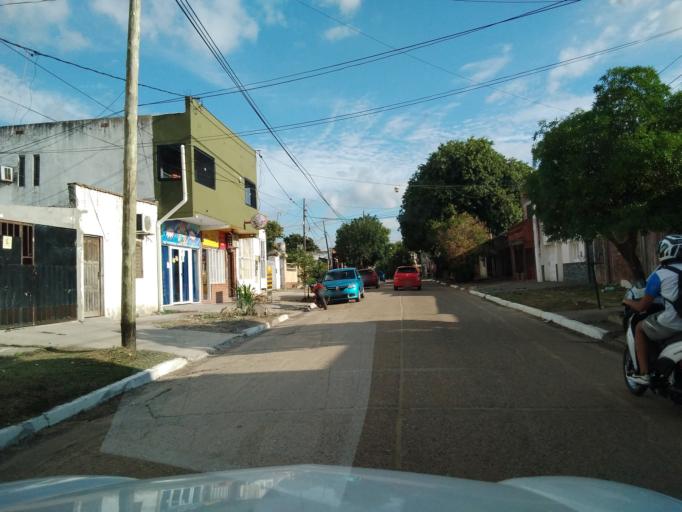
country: AR
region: Corrientes
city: Corrientes
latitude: -27.4601
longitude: -58.8191
